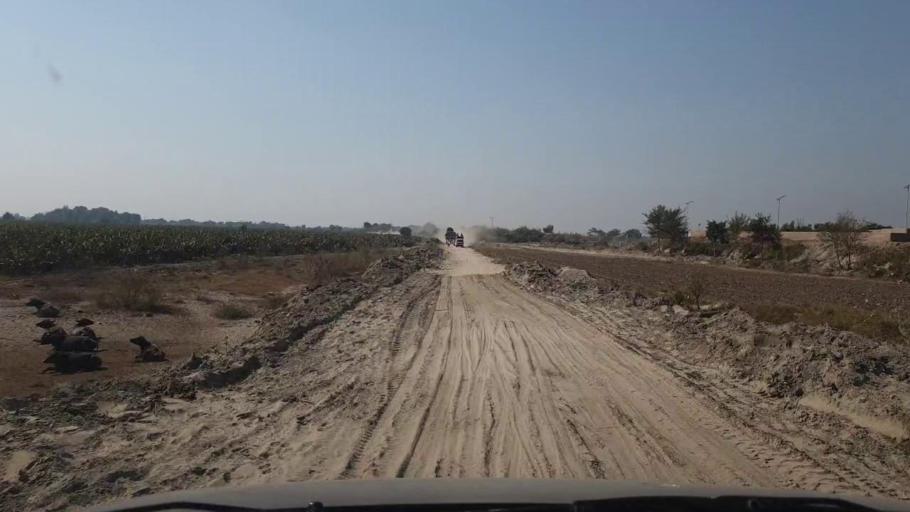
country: PK
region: Sindh
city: Tando Allahyar
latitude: 25.4366
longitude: 68.6444
